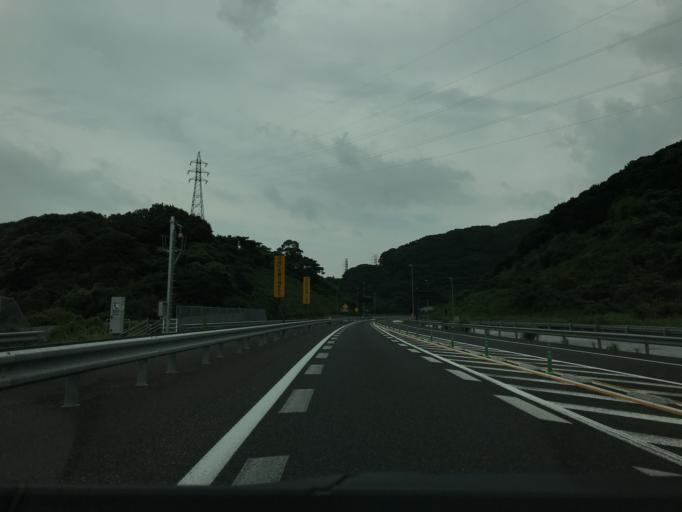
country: JP
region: Fukuoka
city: Kanda
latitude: 33.7947
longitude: 130.9667
